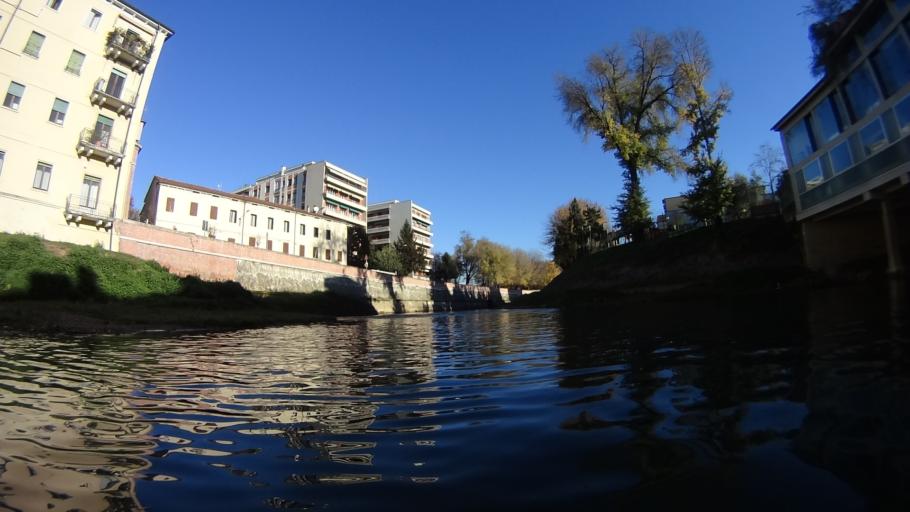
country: IT
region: Veneto
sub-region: Provincia di Vicenza
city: Vicenza
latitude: 45.5510
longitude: 11.5449
